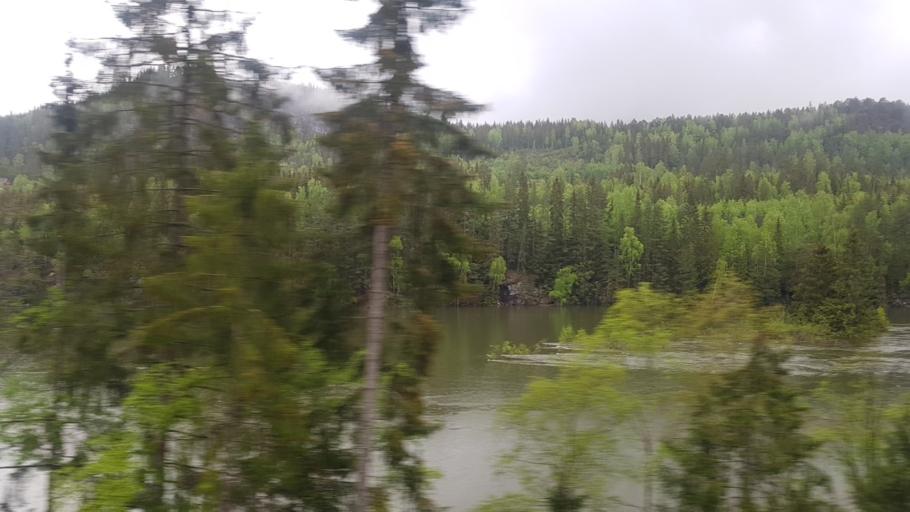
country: NO
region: Oppland
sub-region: Oyer
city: Tretten
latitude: 61.2769
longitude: 10.3773
